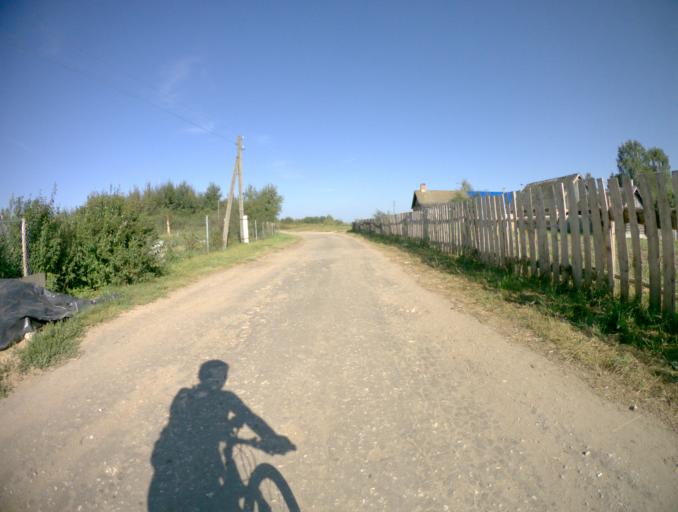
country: RU
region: Vladimir
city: Orgtrud
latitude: 56.3132
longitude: 40.6131
